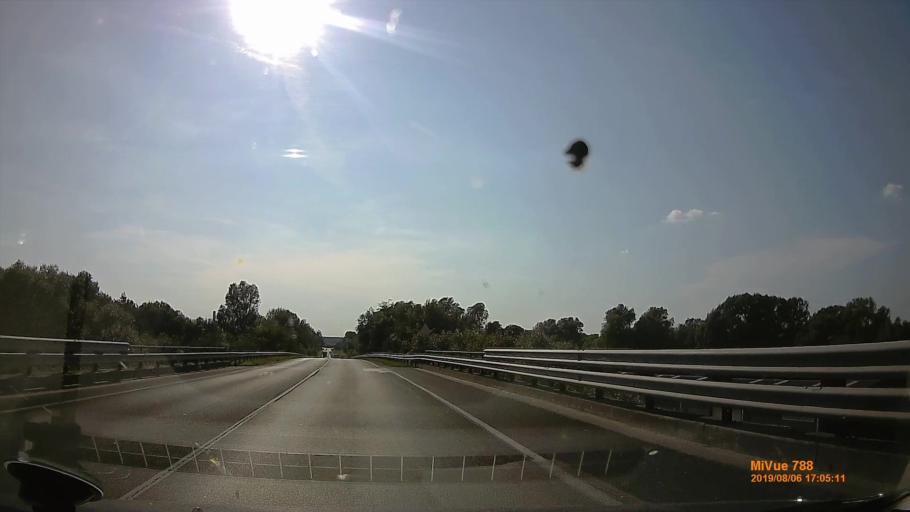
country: HU
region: Zala
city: Nagykanizsa
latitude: 46.4670
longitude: 16.9801
